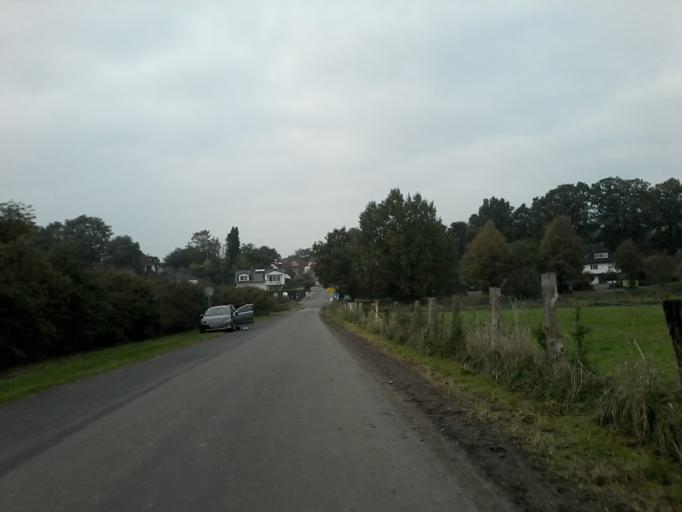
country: DE
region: Lower Saxony
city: Ahsen-Oetzen
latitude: 52.9959
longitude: 9.0864
